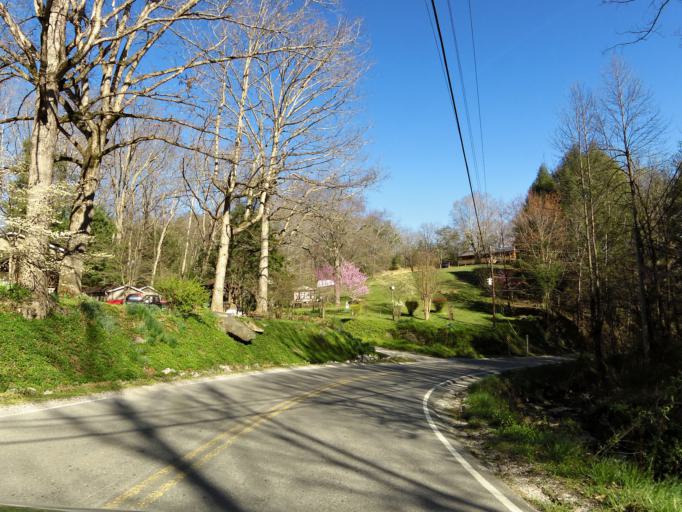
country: US
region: Tennessee
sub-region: Scott County
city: Huntsville
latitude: 36.3753
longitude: -84.3927
